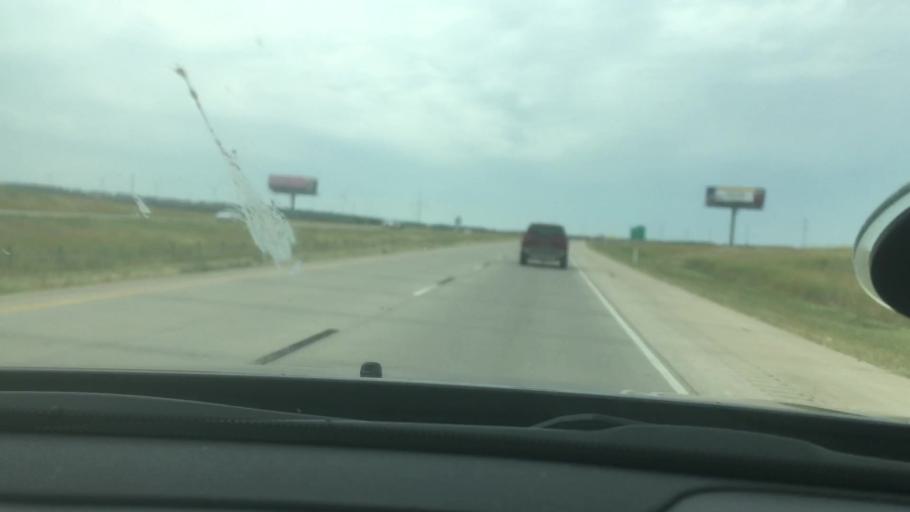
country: US
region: Oklahoma
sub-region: Carter County
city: Ardmore
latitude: 34.3261
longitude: -97.1546
